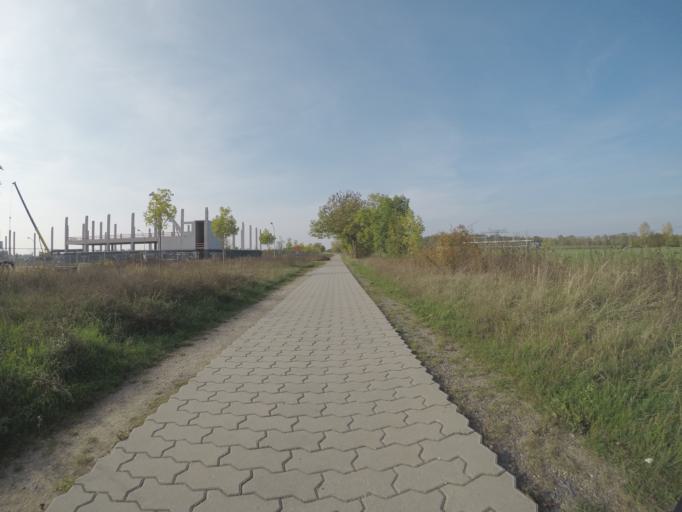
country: DE
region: Brandenburg
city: Schonefeld
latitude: 52.3925
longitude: 13.4909
